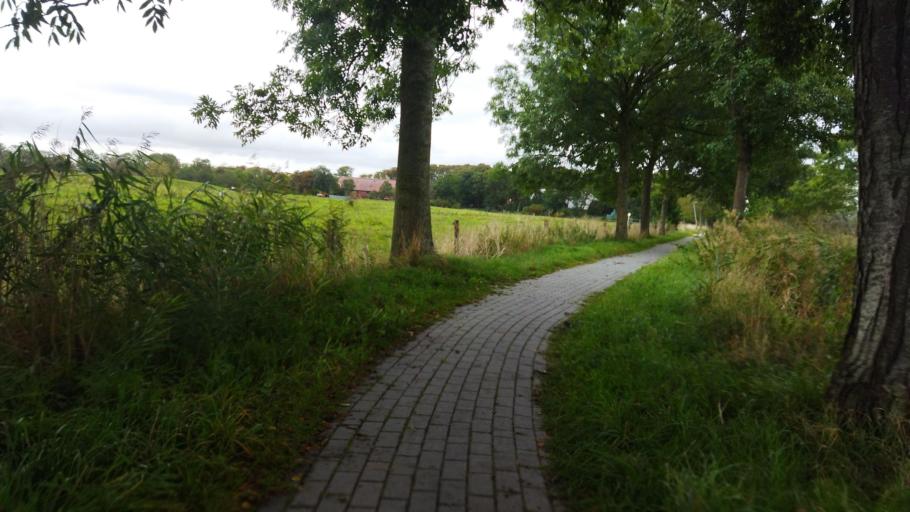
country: DE
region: Lower Saxony
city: Hinte
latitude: 53.4254
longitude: 7.1812
